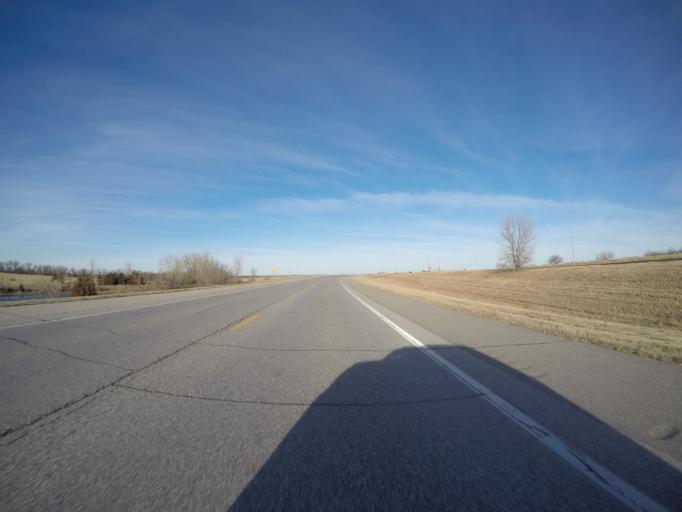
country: US
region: Kansas
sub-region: Marion County
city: Peabody
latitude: 38.1440
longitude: -97.2284
